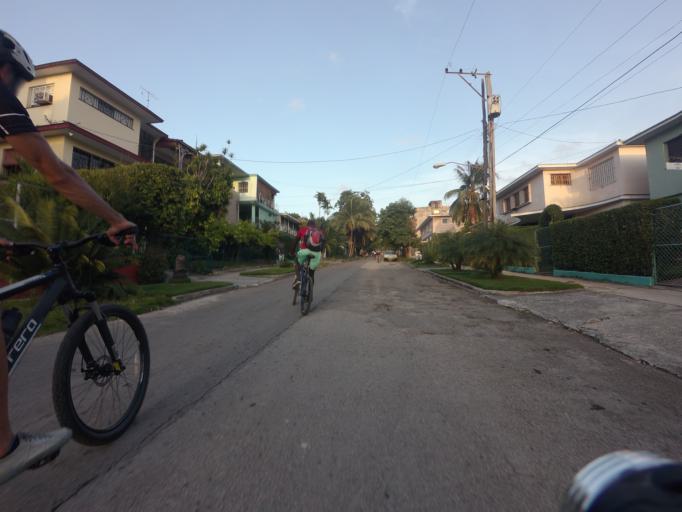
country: CU
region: La Habana
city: Havana
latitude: 23.1164
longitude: -82.4040
